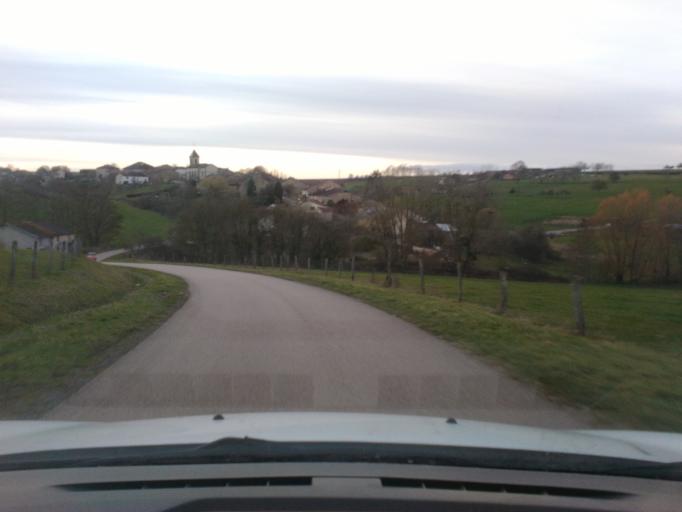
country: FR
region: Lorraine
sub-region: Departement des Vosges
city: Rambervillers
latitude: 48.3544
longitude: 6.5310
